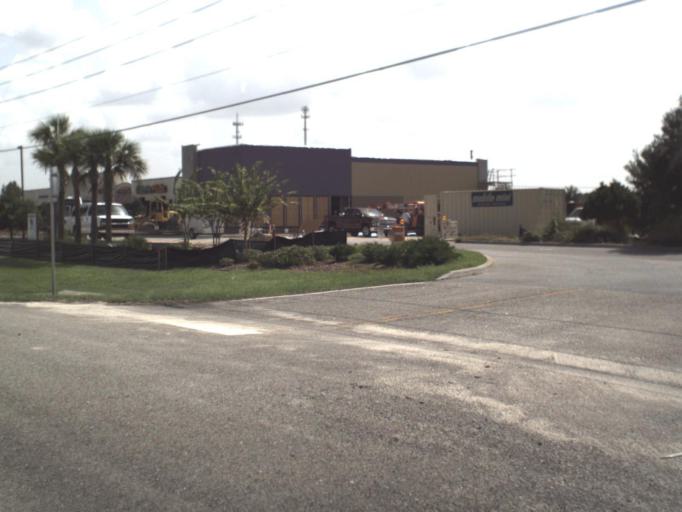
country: US
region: Florida
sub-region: Polk County
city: Dundee
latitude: 27.9601
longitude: -81.6238
